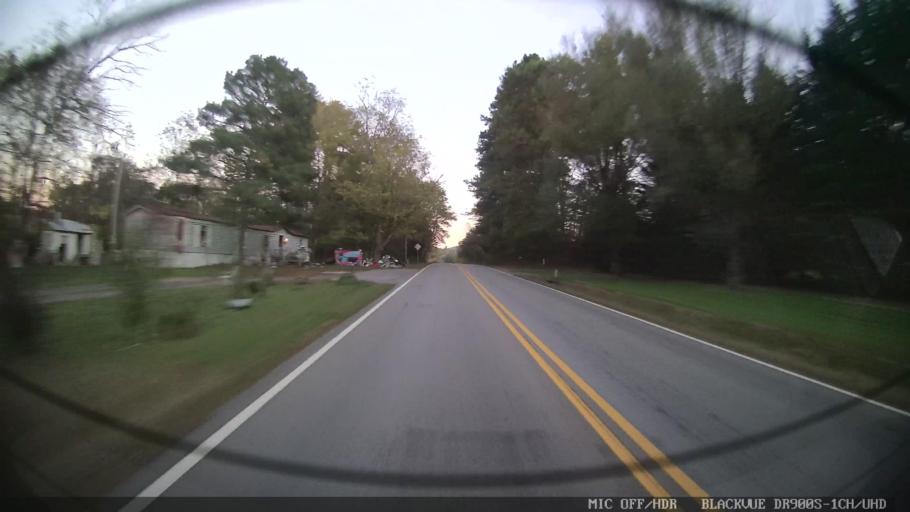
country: US
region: North Carolina
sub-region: Clay County
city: Hayesville
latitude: 34.9701
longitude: -83.8791
